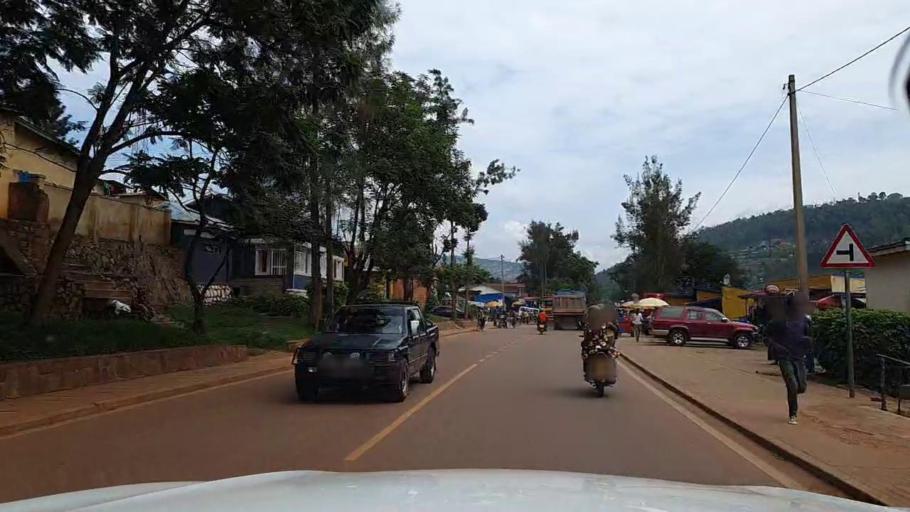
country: RW
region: Kigali
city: Kigali
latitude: -1.9239
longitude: 30.0463
